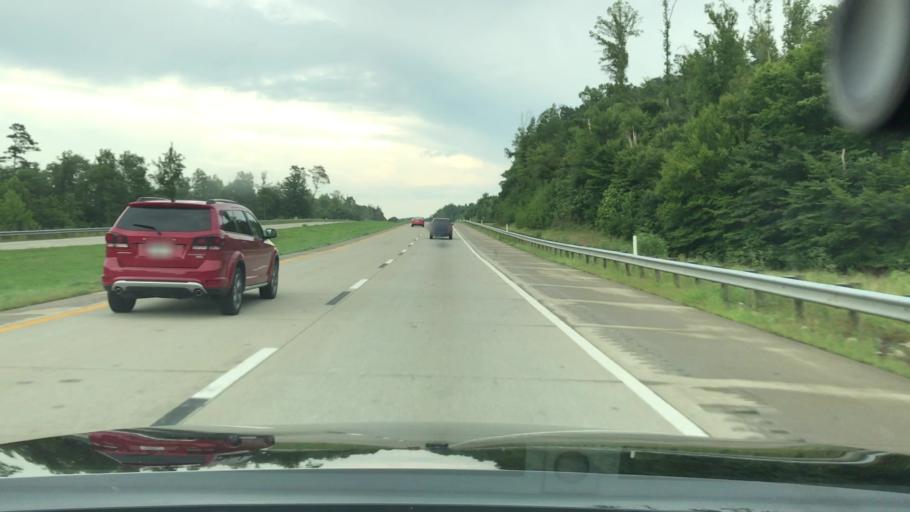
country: US
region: West Virginia
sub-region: Putnam County
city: Eleanor
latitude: 38.5380
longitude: -81.9611
